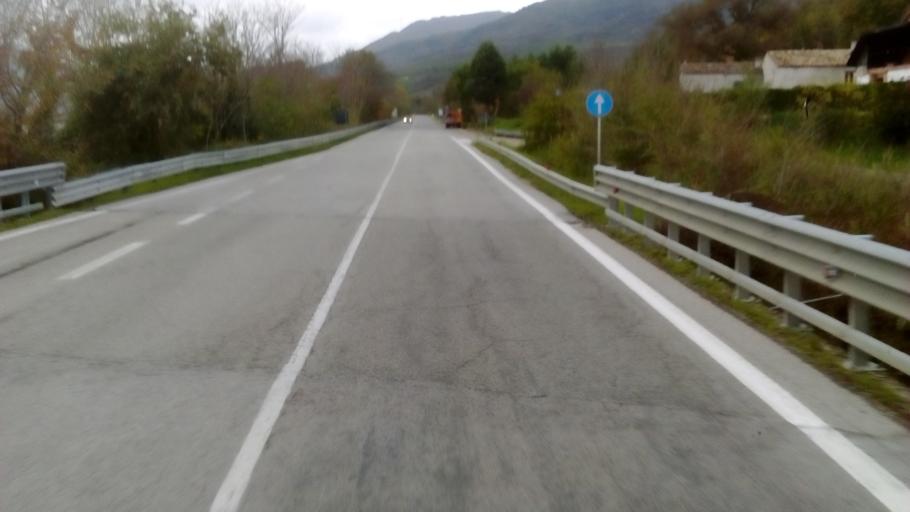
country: IT
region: Abruzzo
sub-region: Provincia di Chieti
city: Tufillo
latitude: 41.8901
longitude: 14.6114
